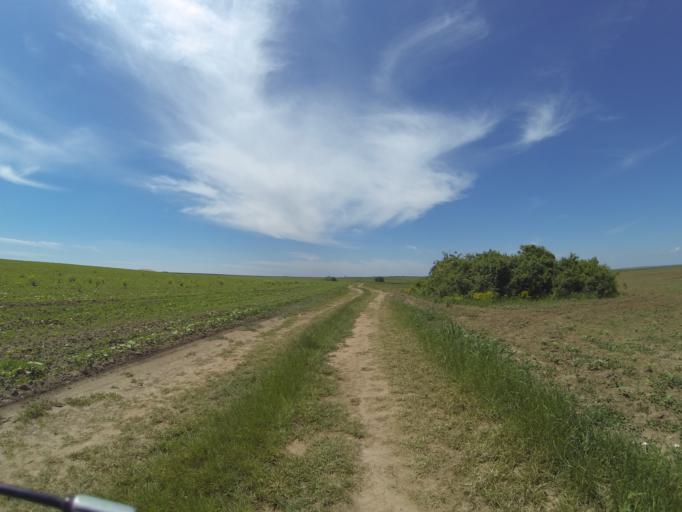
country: RO
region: Dolj
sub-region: Comuna Teslui
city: Teslui
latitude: 44.1908
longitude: 24.1515
